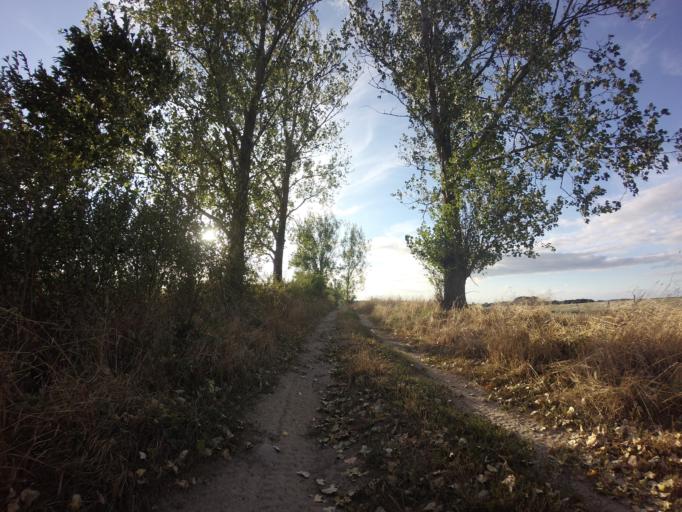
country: PL
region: West Pomeranian Voivodeship
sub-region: Powiat choszczenski
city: Choszczno
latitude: 53.1154
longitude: 15.4300
